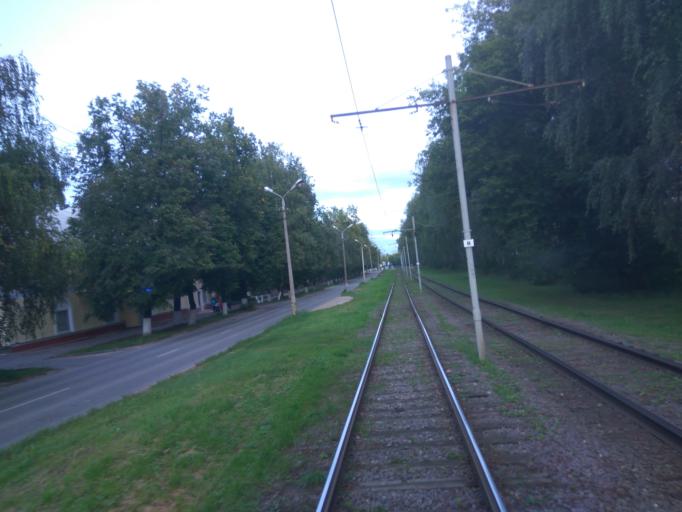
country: RU
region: Moskovskaya
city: Kolomna
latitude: 55.0736
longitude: 38.7884
